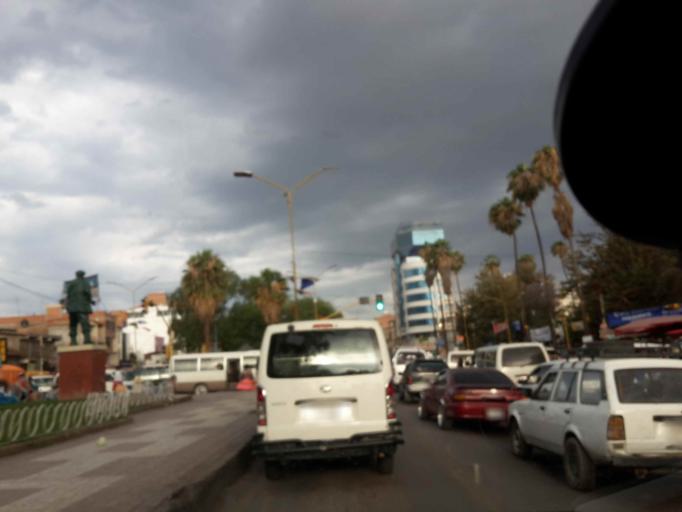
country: BO
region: Cochabamba
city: Sipe Sipe
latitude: -17.3943
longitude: -66.2827
